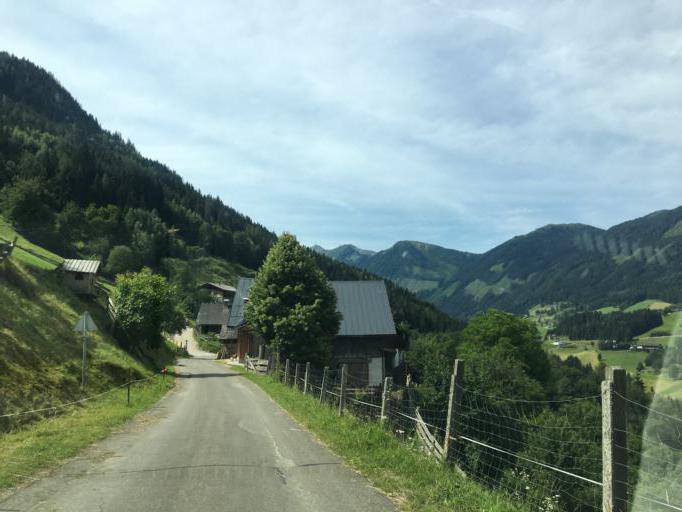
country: AT
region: Styria
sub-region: Politischer Bezirk Liezen
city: Schladming
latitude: 47.3834
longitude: 13.6859
